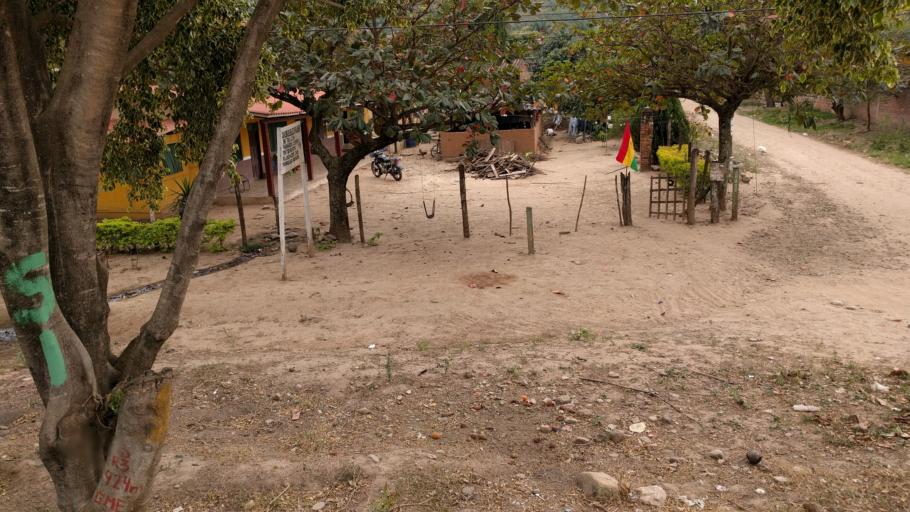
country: BO
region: Santa Cruz
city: Jorochito
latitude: -18.1603
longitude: -63.5045
